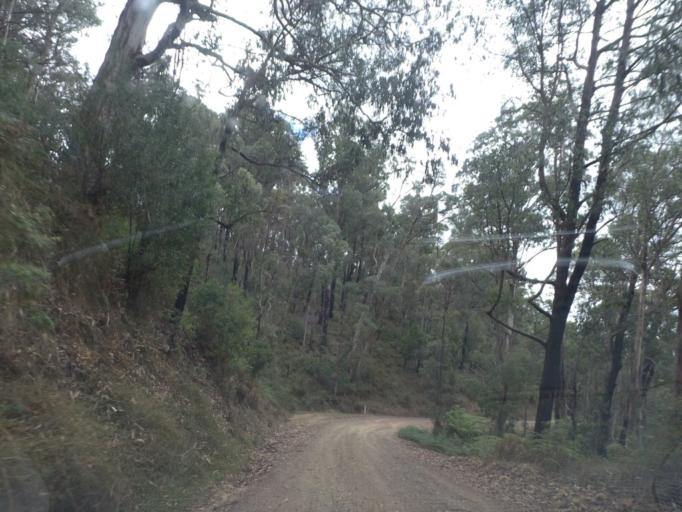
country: AU
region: Victoria
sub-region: Murrindindi
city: Alexandra
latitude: -37.4450
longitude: 145.9650
